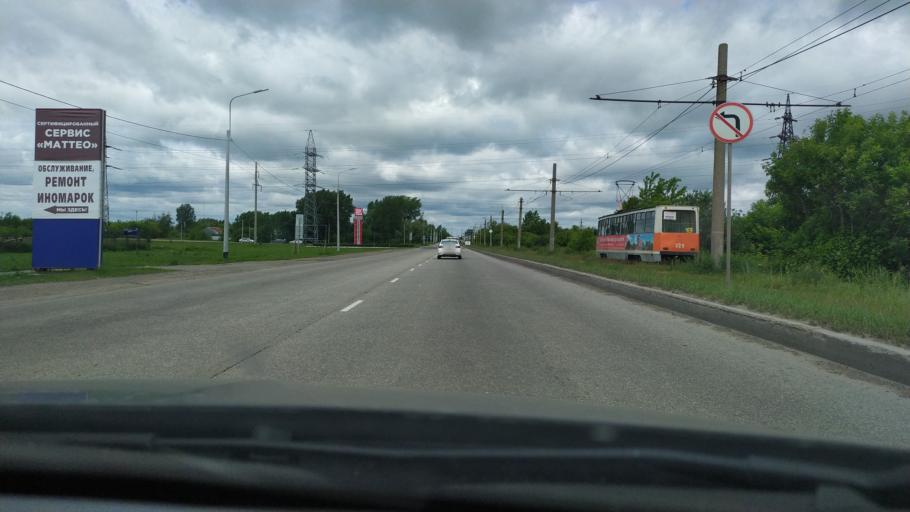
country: RU
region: Perm
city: Kondratovo
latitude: 57.9307
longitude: 56.1284
